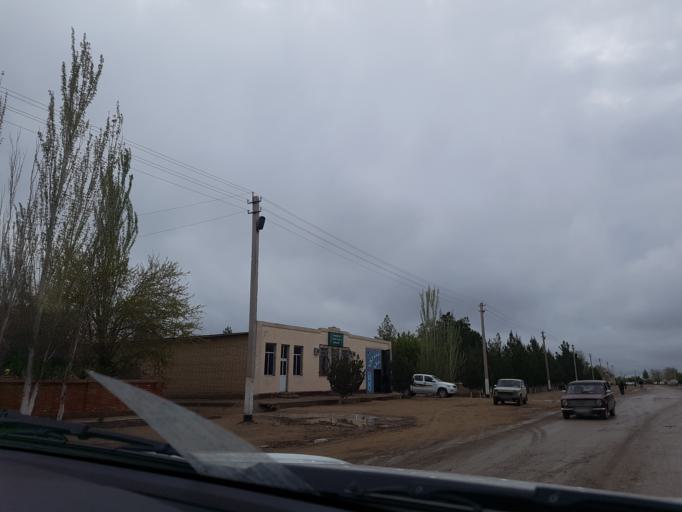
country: TM
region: Lebap
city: Sayat
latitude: 38.4549
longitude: 64.3801
